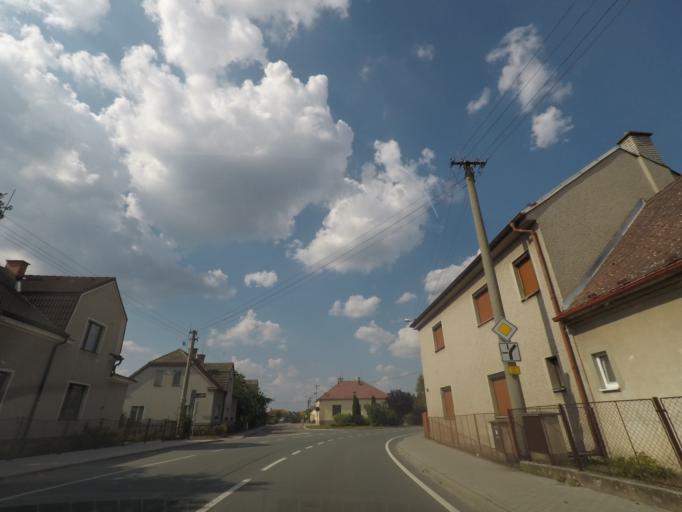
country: CZ
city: Albrechtice nad Orlici
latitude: 50.1432
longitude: 16.0619
